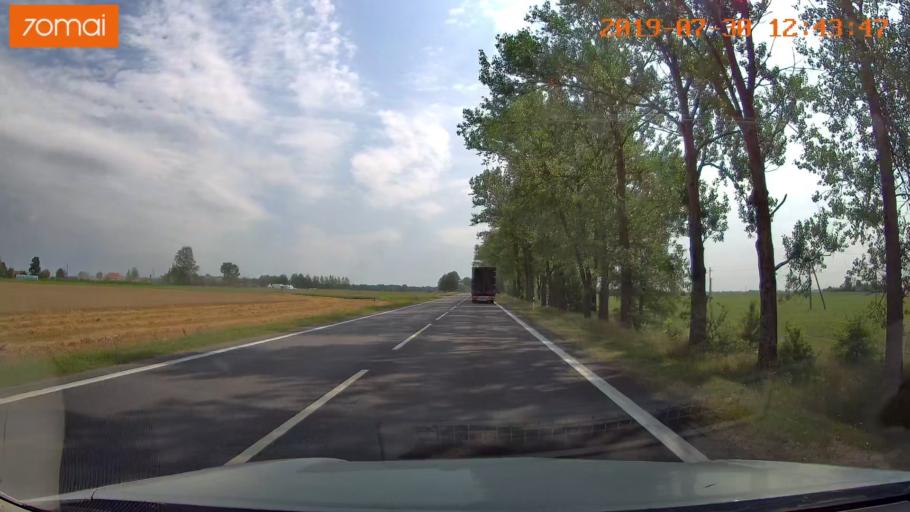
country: LT
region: Marijampoles apskritis
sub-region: Marijampole Municipality
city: Marijampole
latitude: 54.5877
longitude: 23.2463
